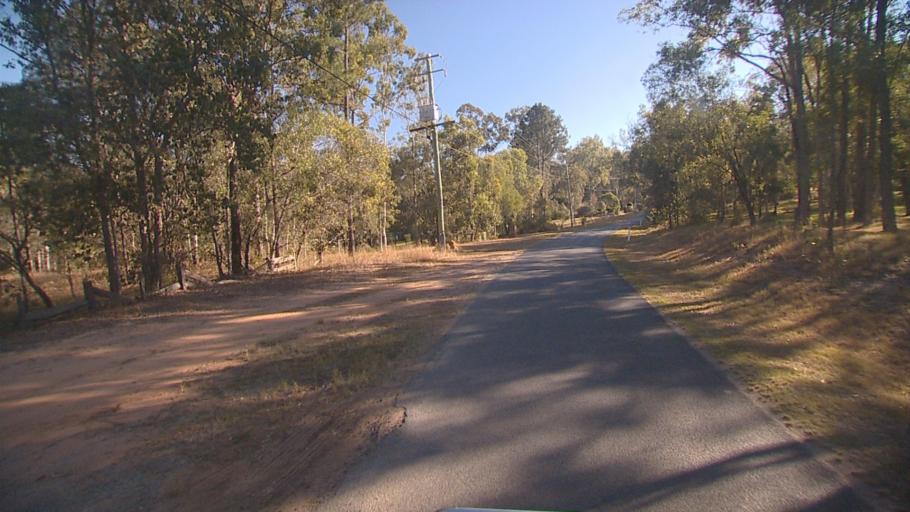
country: AU
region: Queensland
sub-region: Logan
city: North Maclean
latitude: -27.7897
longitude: 152.9610
